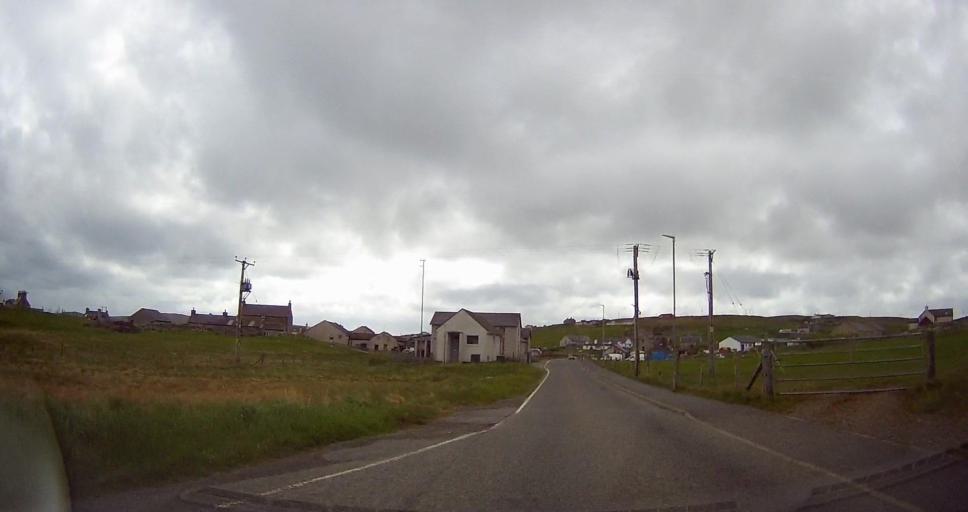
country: GB
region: Scotland
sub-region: Shetland Islands
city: Sandwick
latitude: 60.2302
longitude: -1.5614
